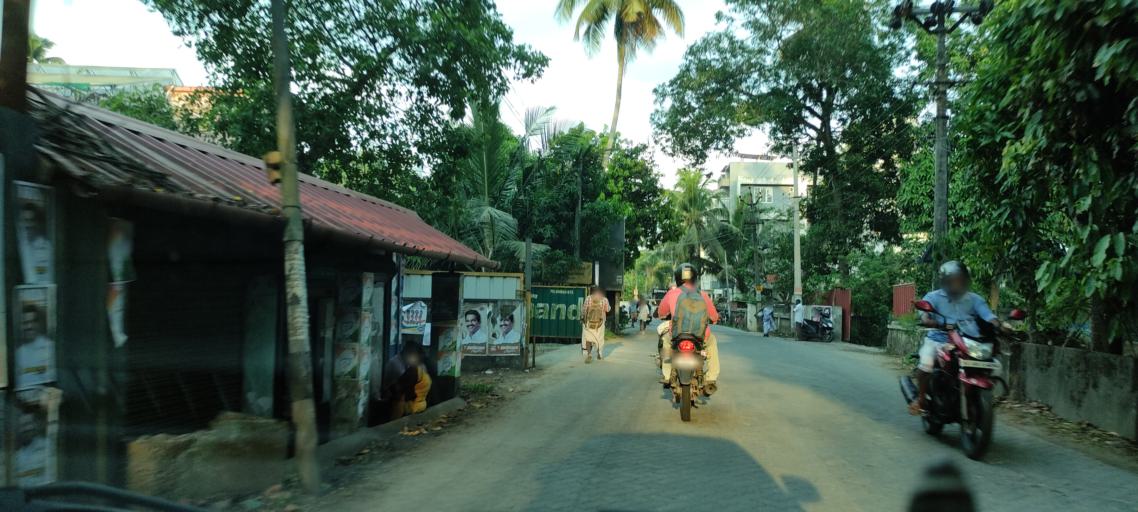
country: IN
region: Kerala
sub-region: Alappuzha
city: Arukutti
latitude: 9.8687
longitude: 76.3094
